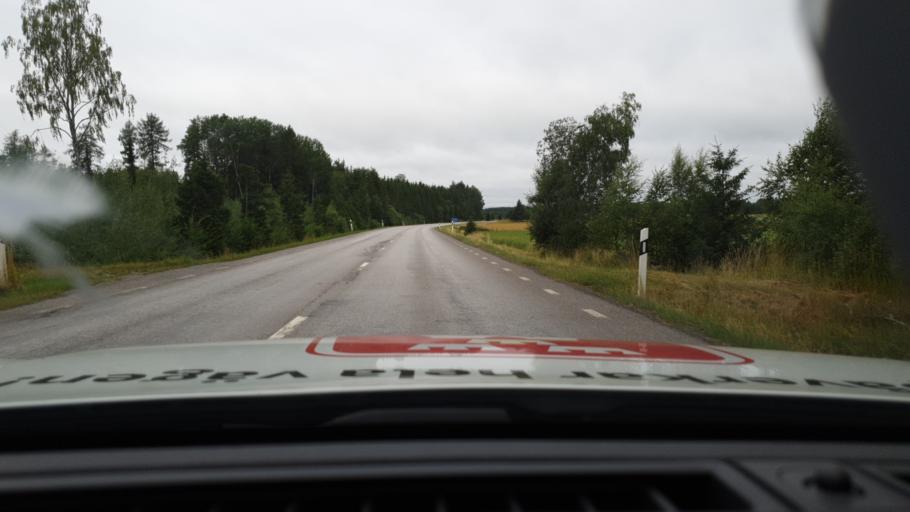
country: SE
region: Uppsala
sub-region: Osthammars Kommun
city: Osterbybruk
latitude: 60.1614
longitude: 17.9968
